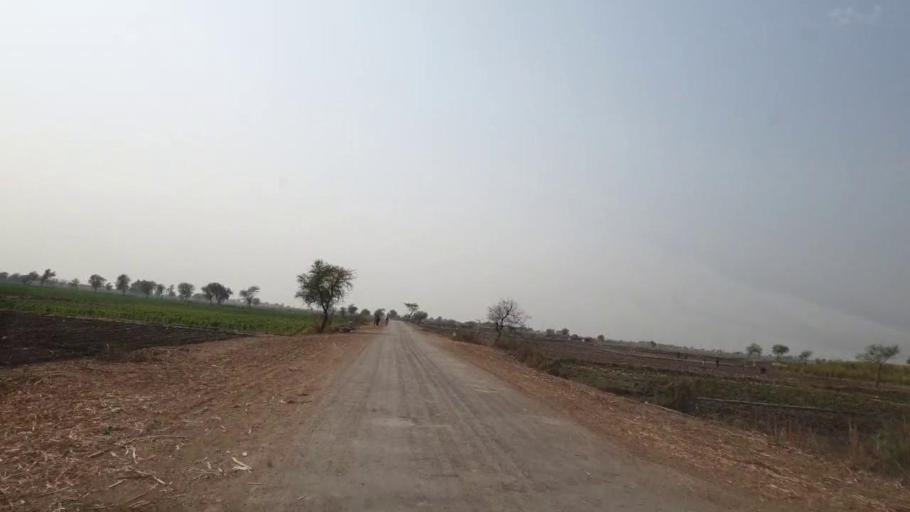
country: PK
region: Sindh
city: Mirpur Khas
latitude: 25.5287
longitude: 69.1544
